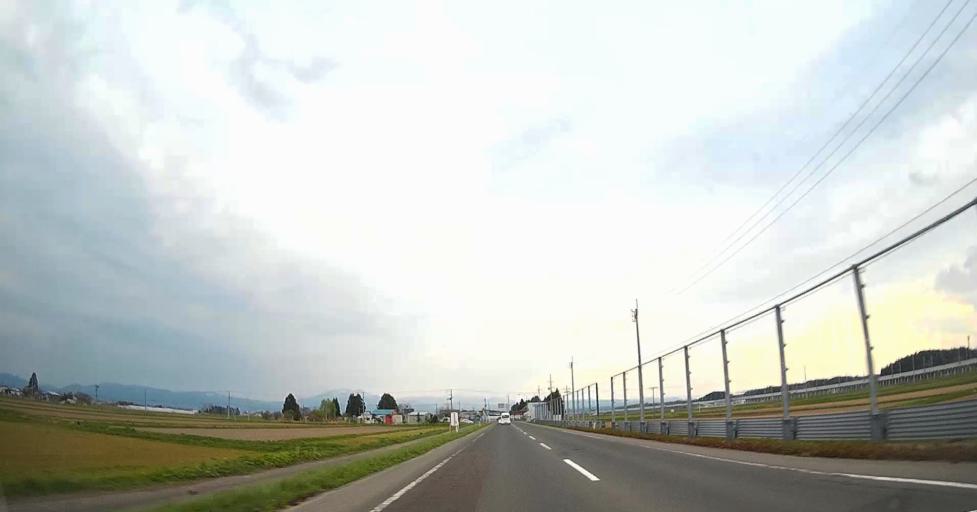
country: JP
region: Aomori
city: Aomori Shi
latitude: 40.8713
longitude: 140.6748
